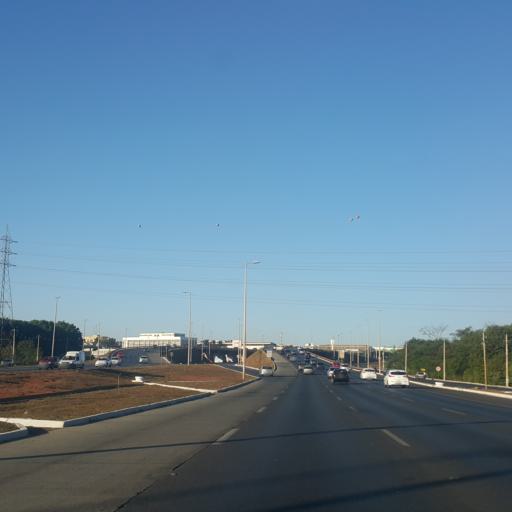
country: BR
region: Federal District
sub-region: Brasilia
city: Brasilia
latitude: -15.8088
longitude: -47.9717
